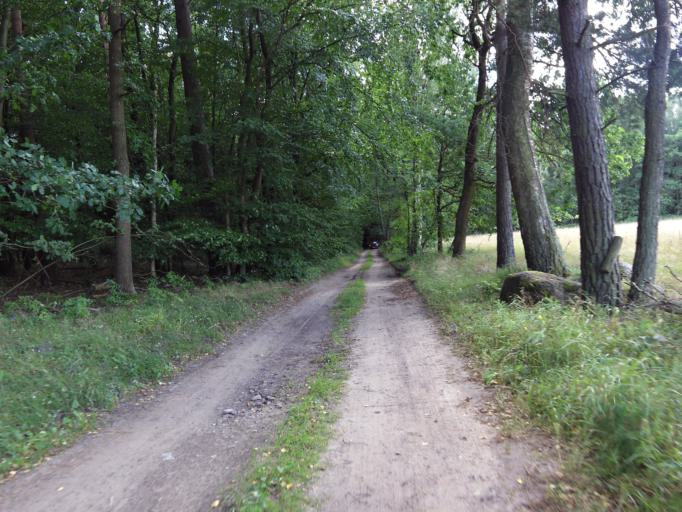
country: DE
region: Brandenburg
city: Lychen
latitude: 53.2639
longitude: 13.4433
